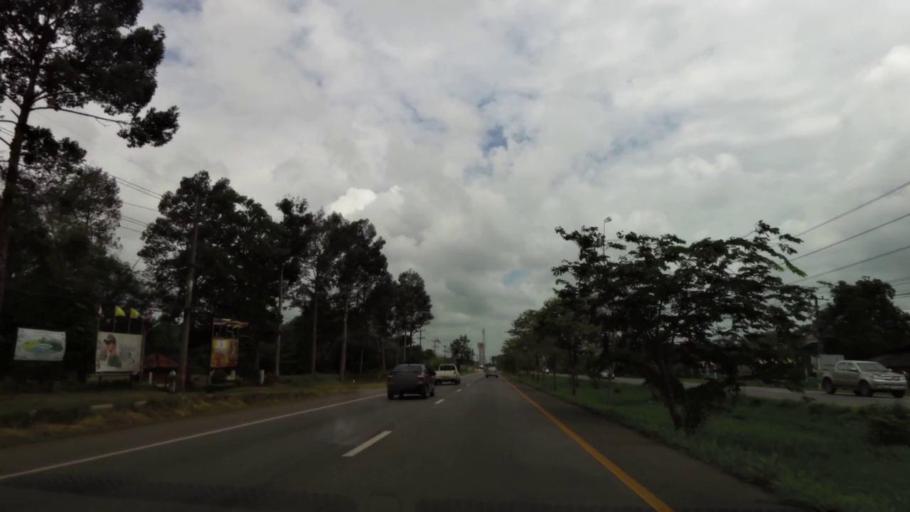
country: TH
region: Chanthaburi
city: Na Yai Am
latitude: 12.7539
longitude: 101.8648
